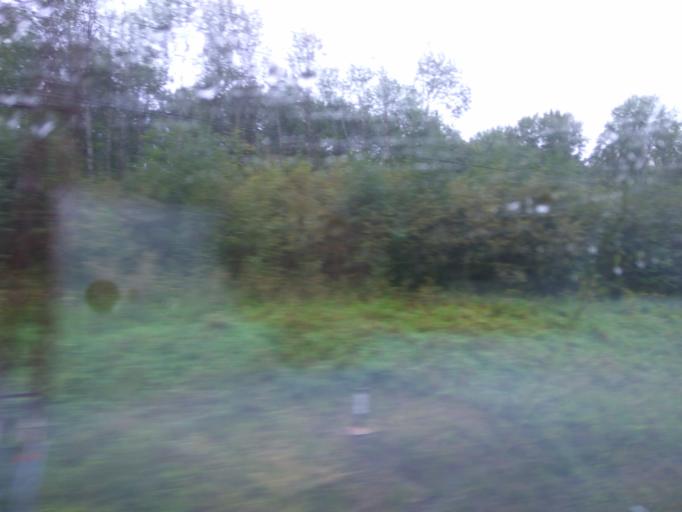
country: RU
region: Moskovskaya
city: Zhilevo
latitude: 55.0198
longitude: 38.0133
